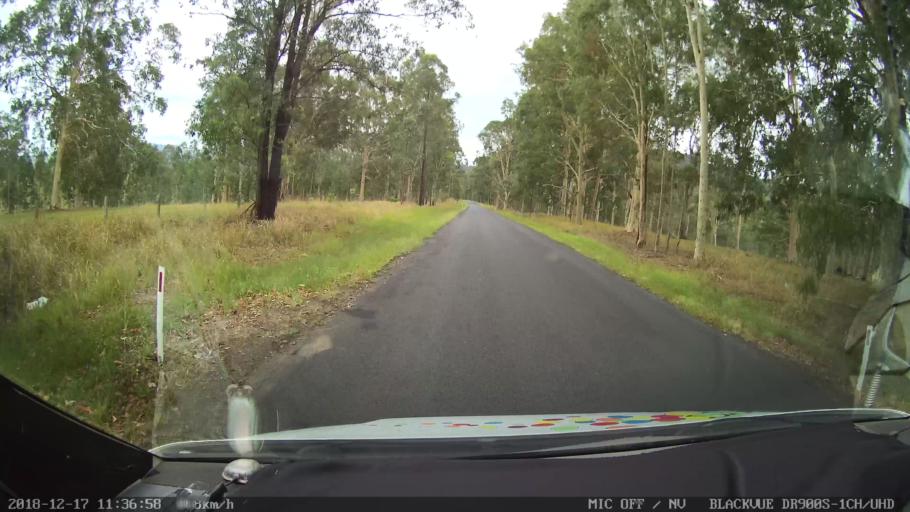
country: AU
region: New South Wales
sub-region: Kyogle
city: Kyogle
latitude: -28.7090
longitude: 152.6062
